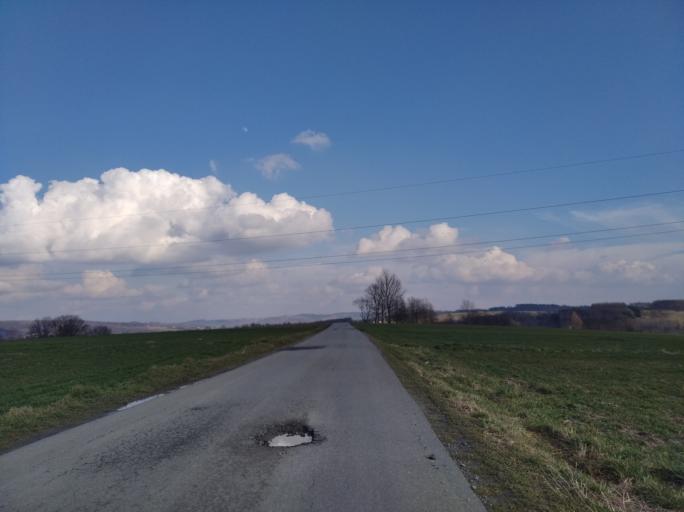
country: PL
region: Subcarpathian Voivodeship
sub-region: Powiat strzyzowski
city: Wysoka Strzyzowska
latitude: 49.8636
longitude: 21.7326
